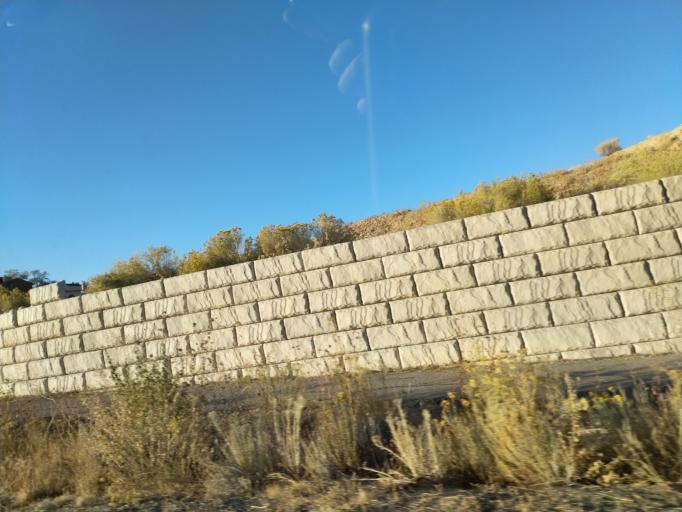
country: US
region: Colorado
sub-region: Mesa County
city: Redlands
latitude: 39.0569
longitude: -108.6162
